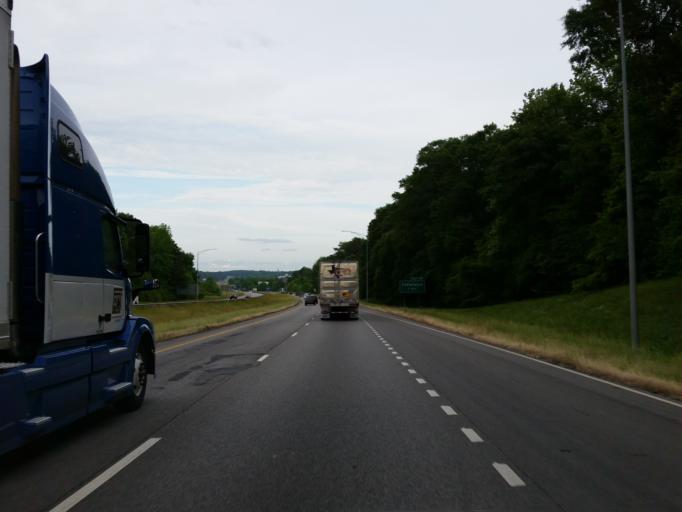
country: US
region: Alabama
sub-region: Tuscaloosa County
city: Holt
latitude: 33.1731
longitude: -87.4692
